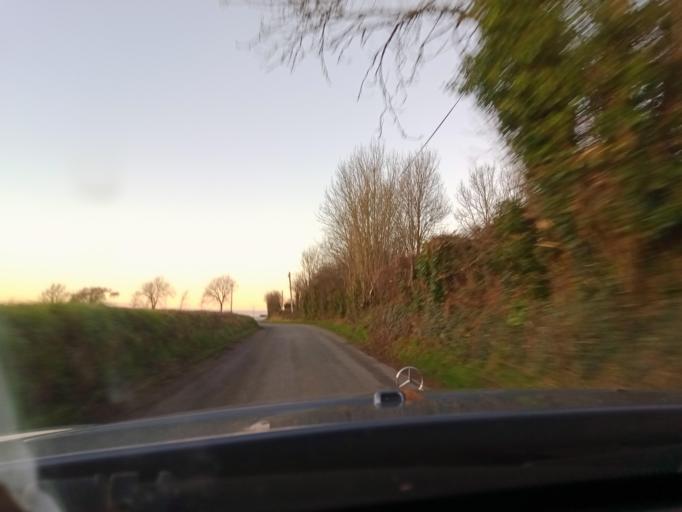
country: IE
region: Leinster
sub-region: Kilkenny
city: Thomastown
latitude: 52.4546
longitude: -7.1052
